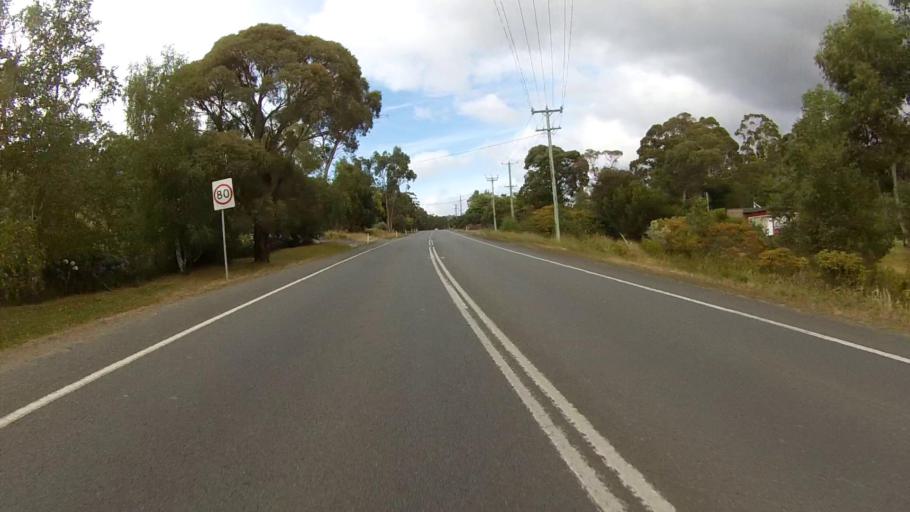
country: AU
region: Tasmania
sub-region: Kingborough
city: Margate
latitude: -43.0763
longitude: 147.2567
